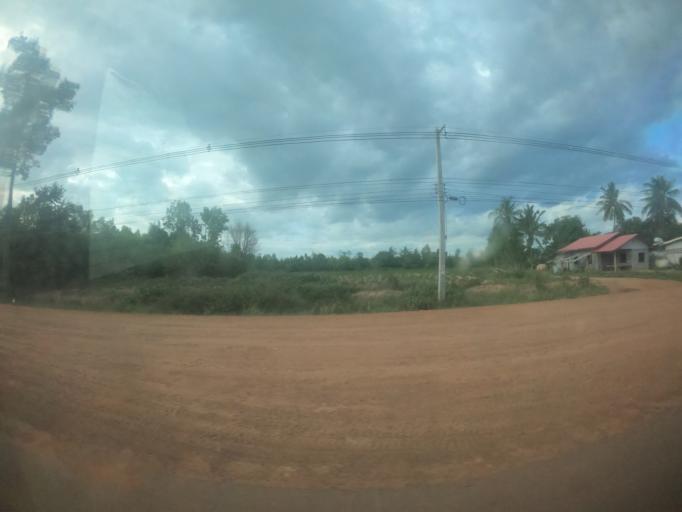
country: TH
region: Surin
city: Kap Choeng
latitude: 14.4610
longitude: 103.6577
